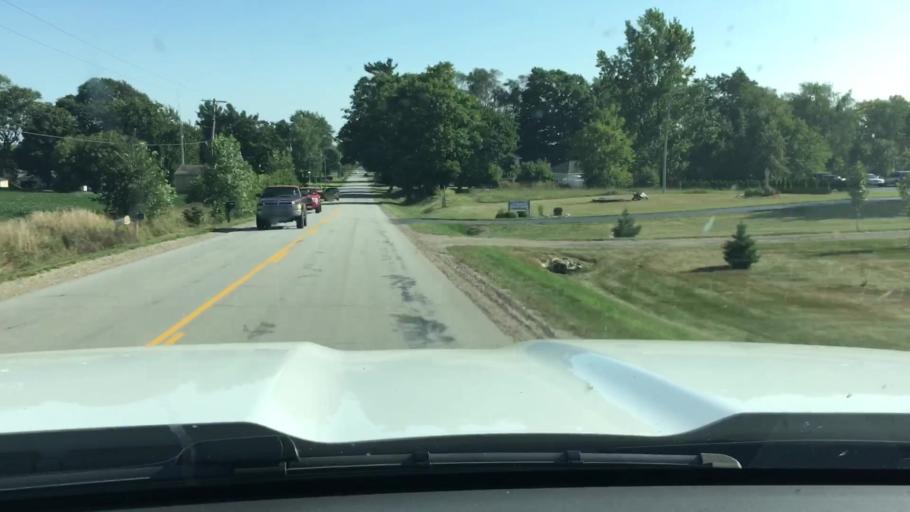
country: US
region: Michigan
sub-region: Ottawa County
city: Zeeland
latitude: 42.8508
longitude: -85.9600
